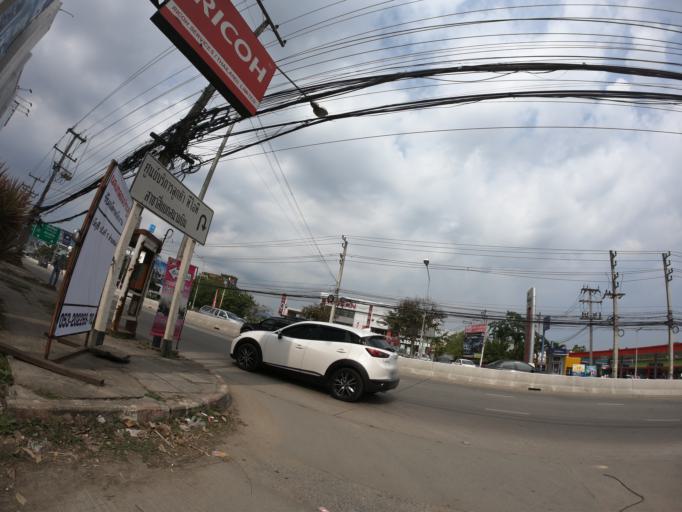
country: TH
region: Chiang Mai
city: Chiang Mai
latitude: 18.7677
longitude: 98.9822
